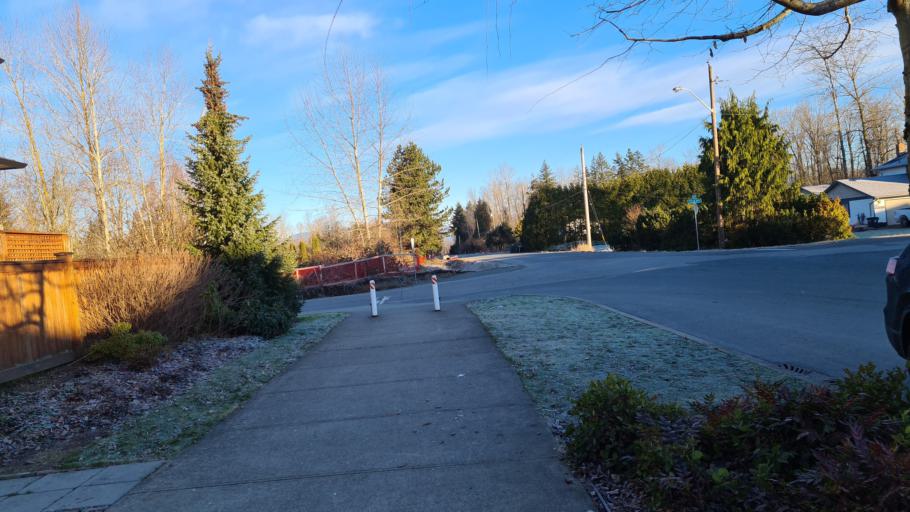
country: CA
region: British Columbia
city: Langley
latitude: 49.1353
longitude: -122.6724
